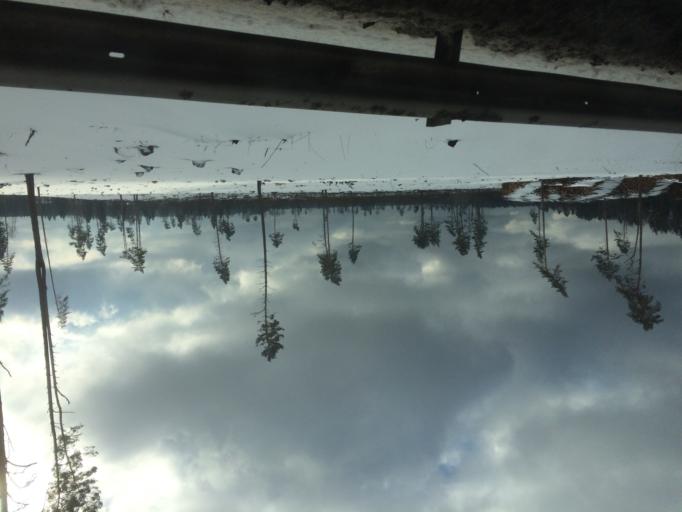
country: RU
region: Moskovskaya
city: Pavlovskaya Sloboda
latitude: 55.7986
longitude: 37.1314
